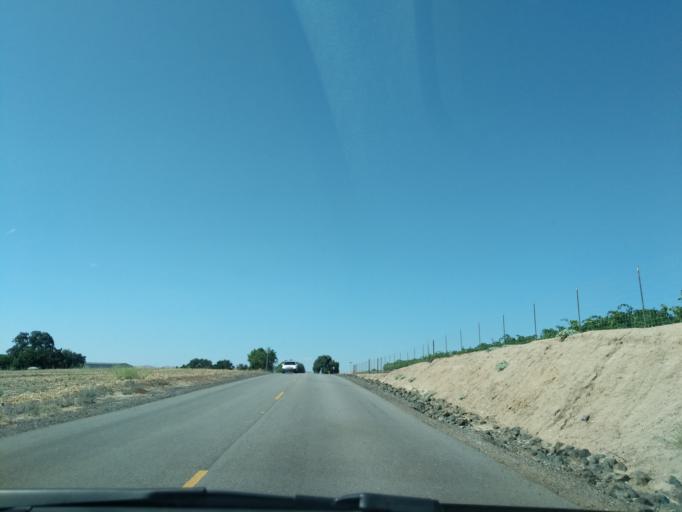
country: US
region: California
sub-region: San Luis Obispo County
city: Paso Robles
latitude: 35.6872
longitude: -120.6408
